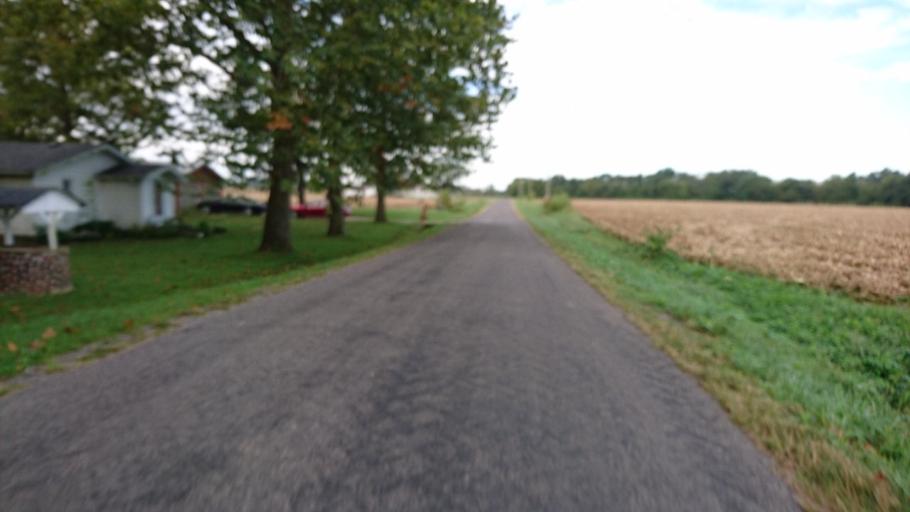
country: US
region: Illinois
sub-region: Macoupin County
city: Staunton
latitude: 38.9902
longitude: -89.7269
